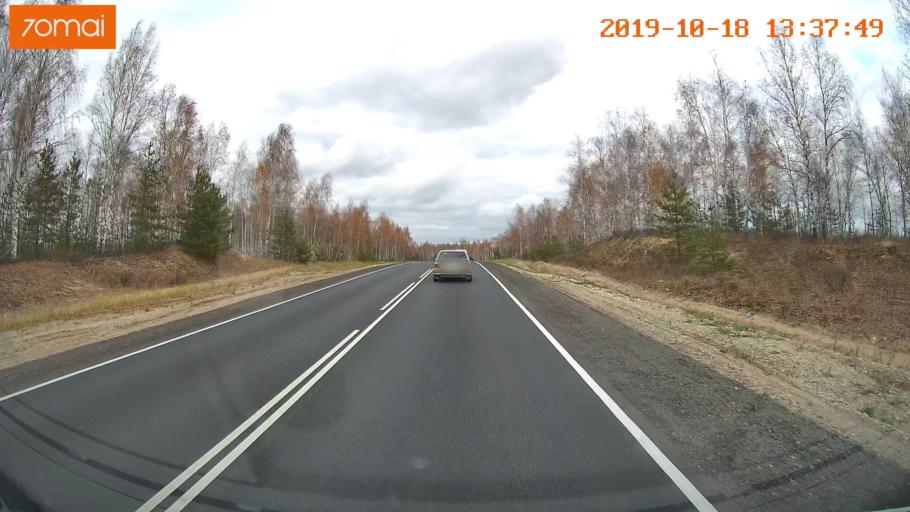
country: RU
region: Rjazan
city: Solotcha
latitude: 54.8831
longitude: 39.9990
